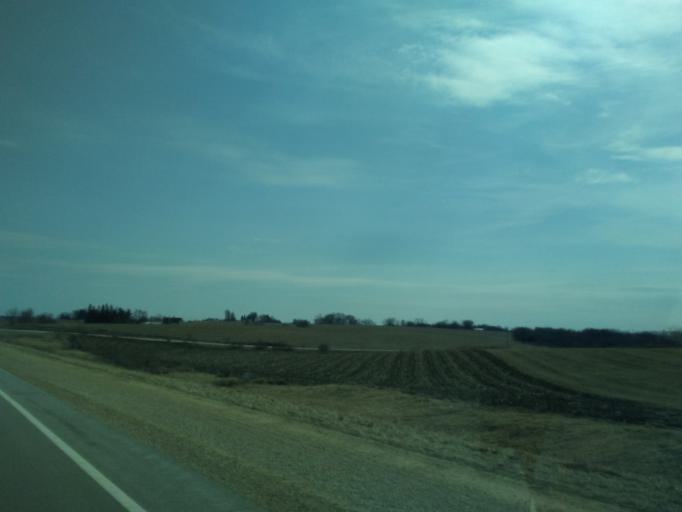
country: US
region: Iowa
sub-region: Winneshiek County
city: Decorah
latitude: 43.4527
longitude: -91.8672
